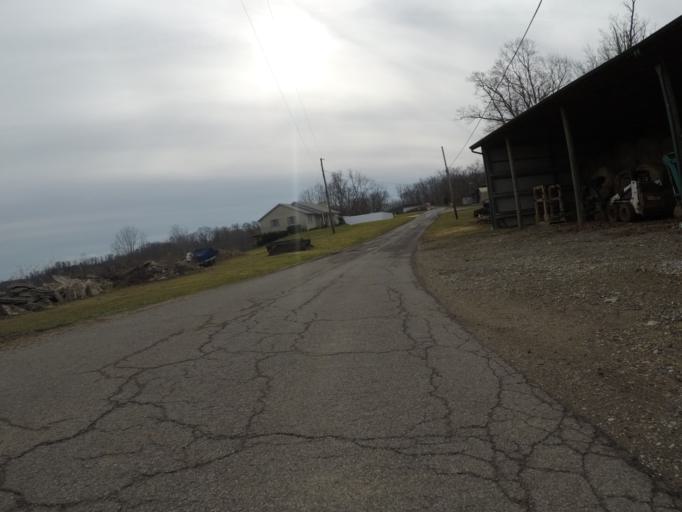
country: US
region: West Virginia
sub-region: Wayne County
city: Lavalette
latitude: 38.3615
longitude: -82.4118
